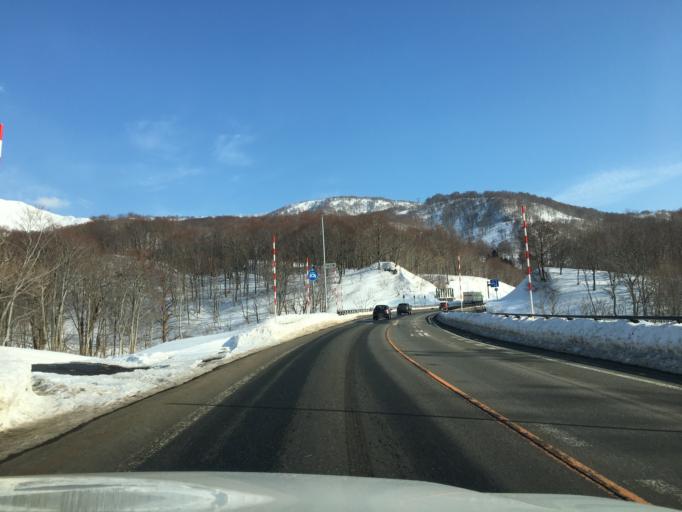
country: JP
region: Yamagata
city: Tsuruoka
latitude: 38.5326
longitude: 139.9491
